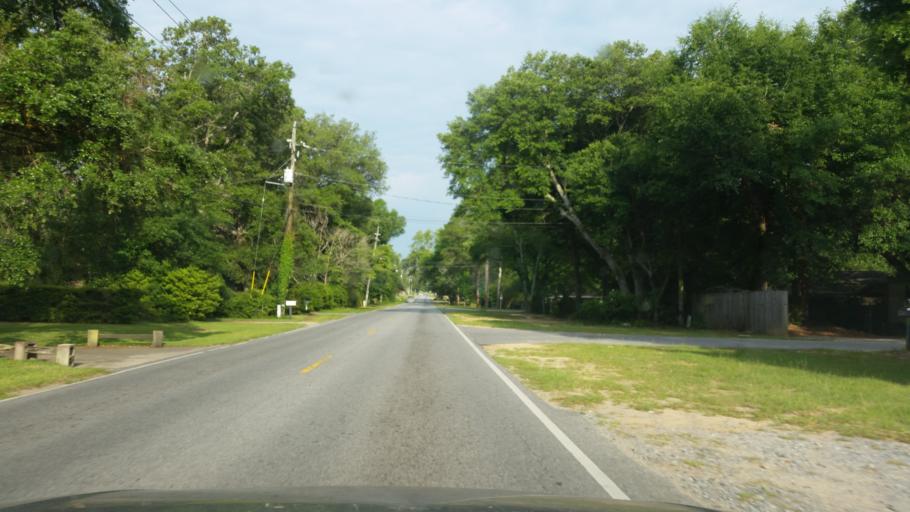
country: US
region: Florida
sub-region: Escambia County
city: Bellview
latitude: 30.4490
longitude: -87.3072
